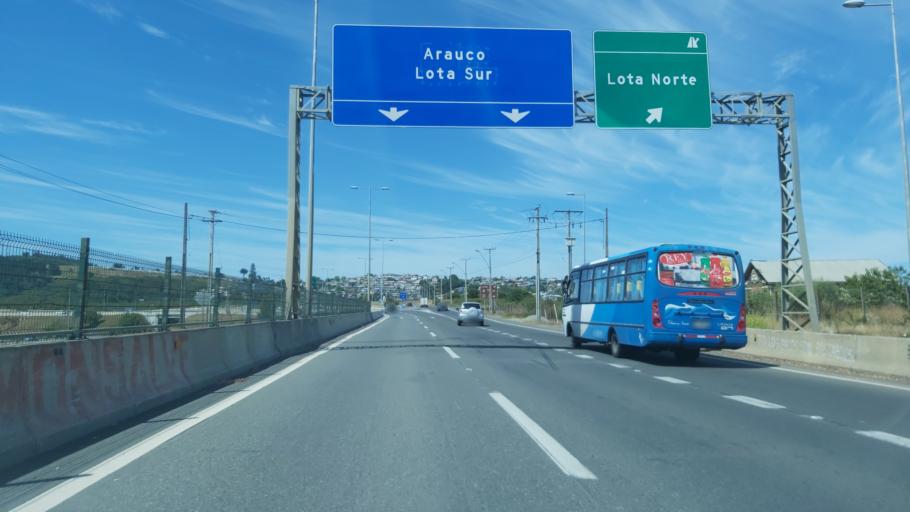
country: CL
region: Biobio
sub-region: Provincia de Concepcion
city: Lota
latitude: -37.0683
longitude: -73.1443
